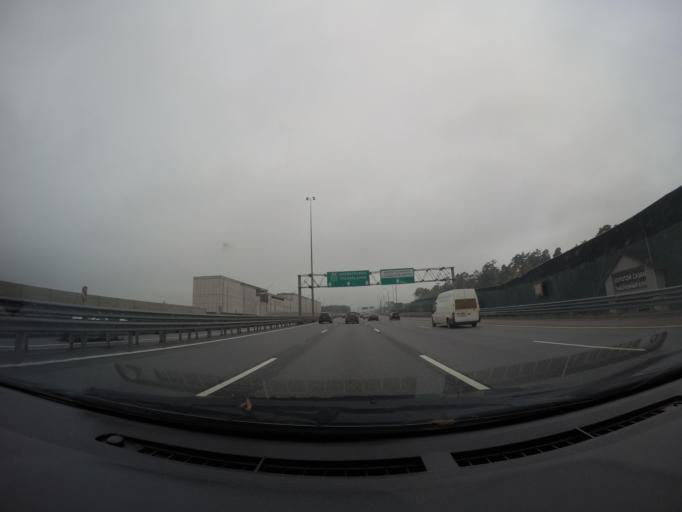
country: RU
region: Moskovskaya
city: Petrovo-Dal'neye
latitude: 55.7754
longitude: 37.1960
